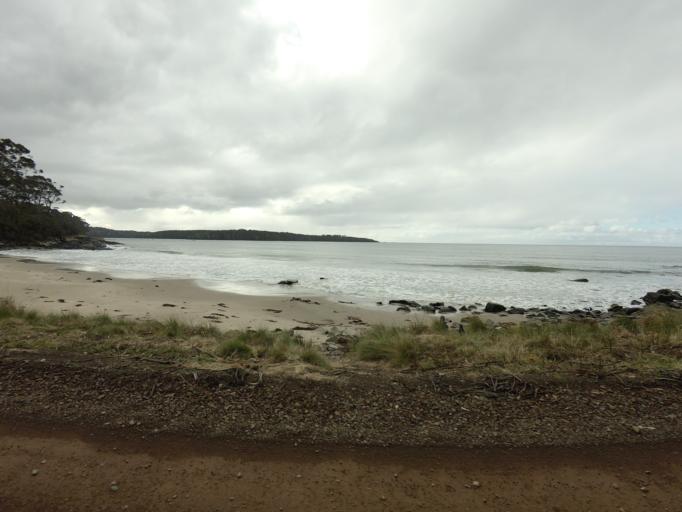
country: AU
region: Tasmania
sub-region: Huon Valley
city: Geeveston
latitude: -43.5455
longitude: 146.8892
